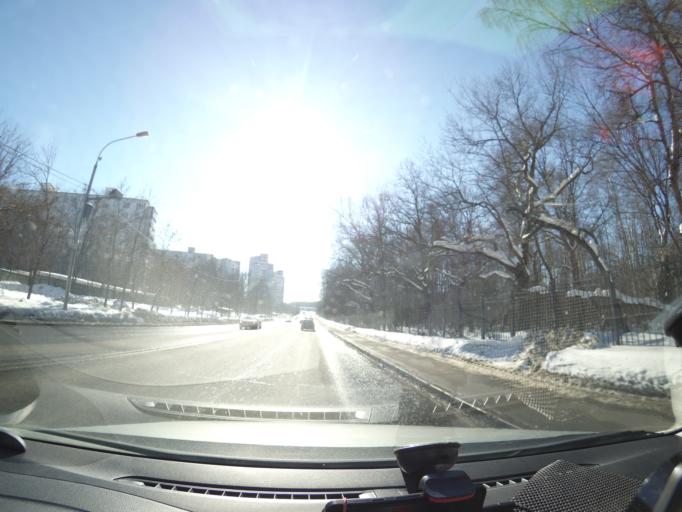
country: RU
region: Moscow
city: Ivanovskoye
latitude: 55.7774
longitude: 37.8192
